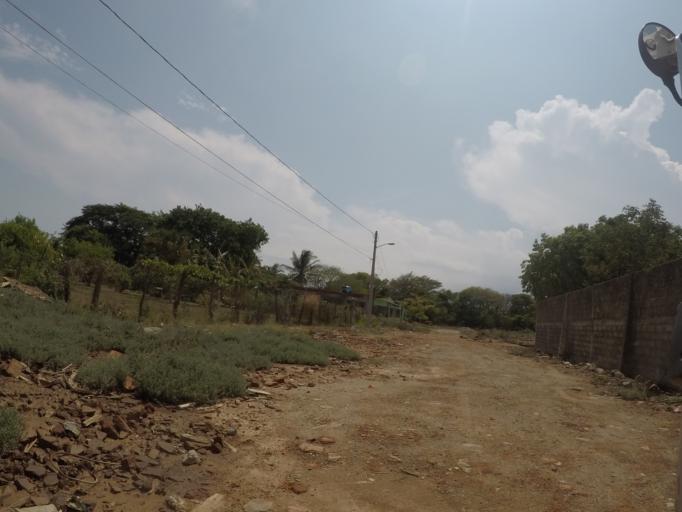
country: MX
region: Oaxaca
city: Union Hidalgo
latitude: 16.4640
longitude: -94.8305
